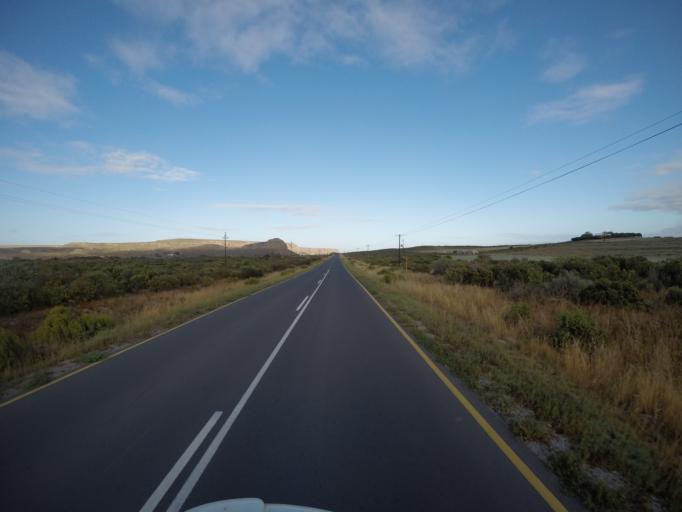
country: ZA
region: Western Cape
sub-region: West Coast District Municipality
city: Clanwilliam
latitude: -32.3120
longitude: 18.3736
